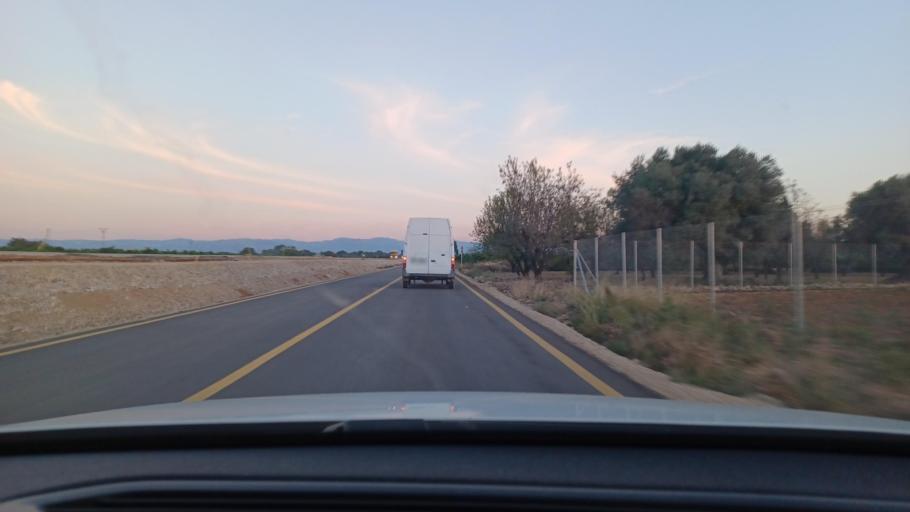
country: ES
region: Catalonia
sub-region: Provincia de Tarragona
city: Alcanar
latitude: 40.5318
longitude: 0.4446
